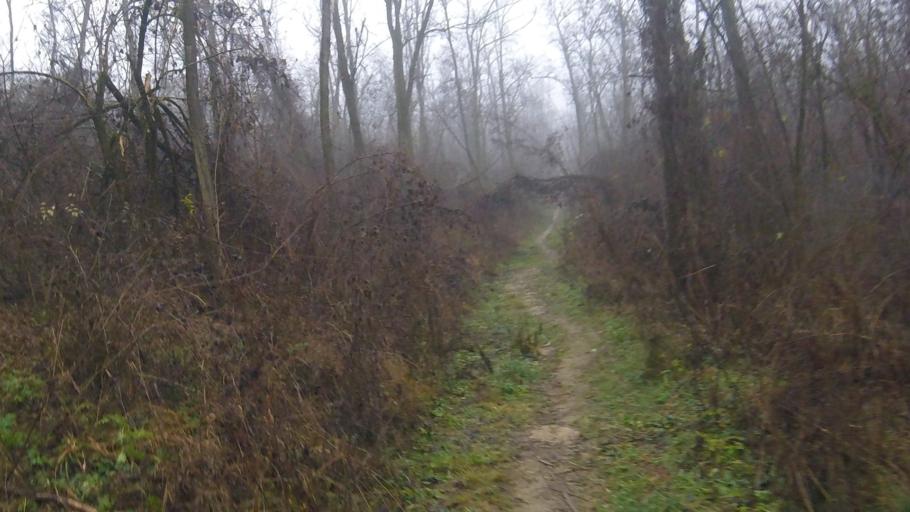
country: HU
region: Pest
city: Biatorbagy
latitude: 47.4692
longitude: 18.8491
